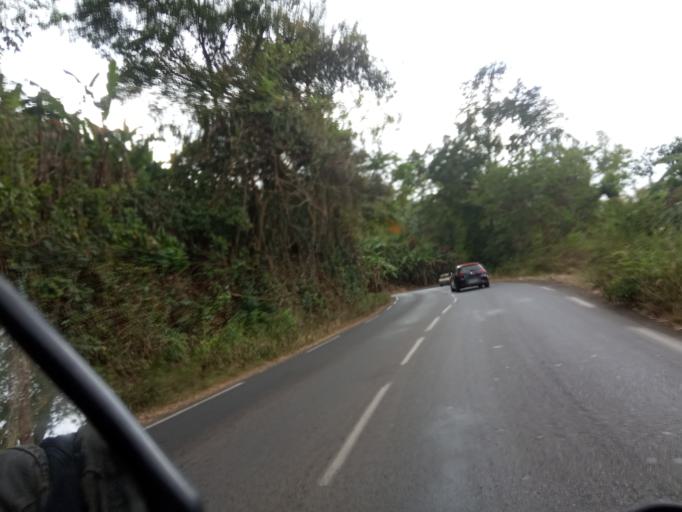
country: YT
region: Dembeni
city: Dembeni
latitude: -12.8366
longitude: 45.1810
